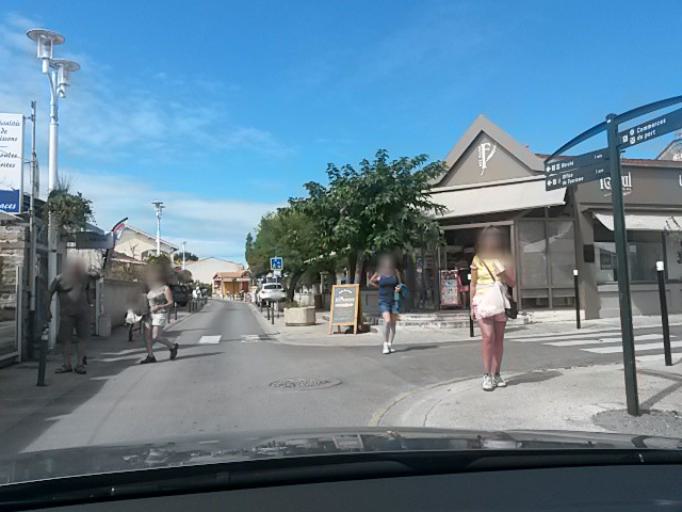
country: FR
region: Poitou-Charentes
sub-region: Departement de la Charente-Maritime
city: Dolus-d'Oleron
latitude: 45.9167
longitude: -1.3296
